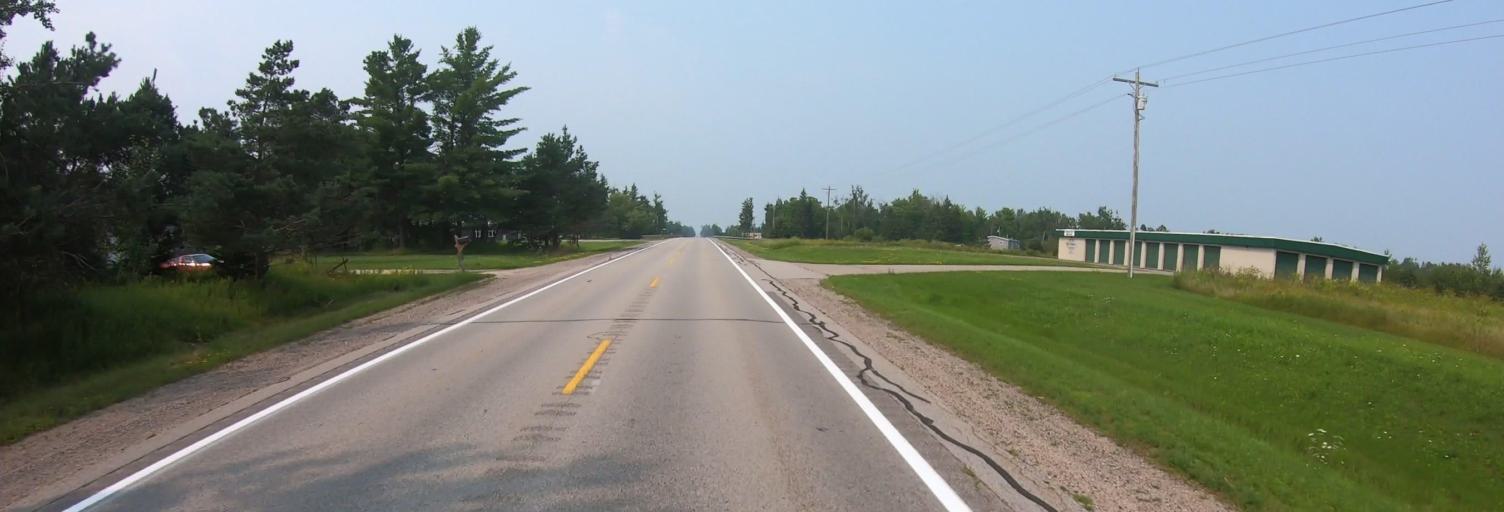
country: US
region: Michigan
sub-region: Chippewa County
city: Sault Ste. Marie
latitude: 46.2282
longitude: -84.3634
